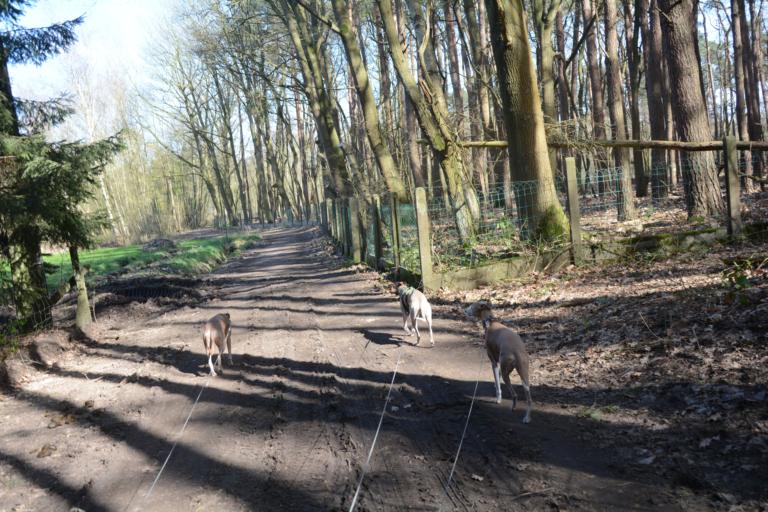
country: BE
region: Flanders
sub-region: Provincie Antwerpen
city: Meerhout
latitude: 51.1440
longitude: 5.0553
